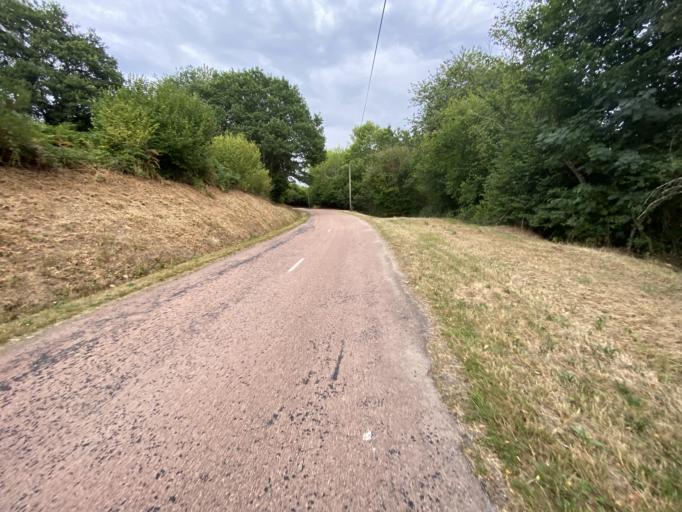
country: FR
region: Bourgogne
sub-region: Departement de la Cote-d'Or
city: Saulieu
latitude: 47.2758
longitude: 4.1483
